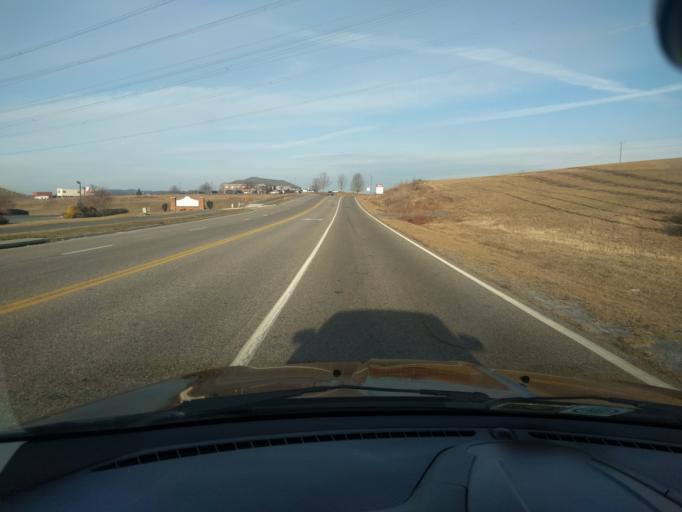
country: US
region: Virginia
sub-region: Augusta County
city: Fishersville
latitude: 38.0889
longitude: -78.9855
